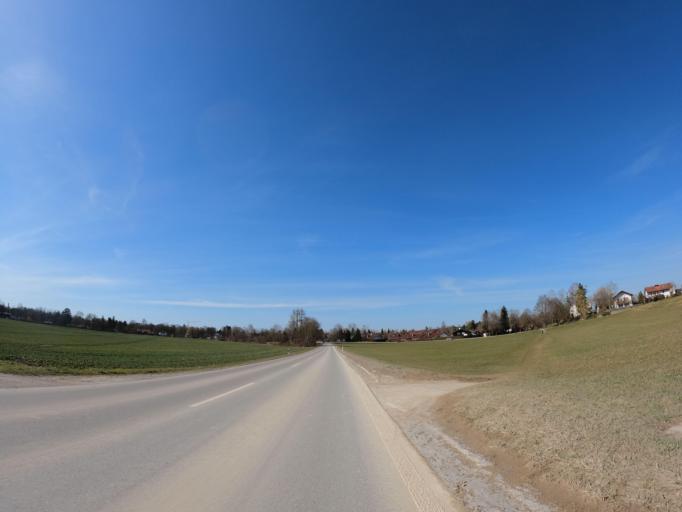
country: DE
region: Bavaria
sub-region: Upper Bavaria
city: Oberhaching
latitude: 48.0219
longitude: 11.6014
